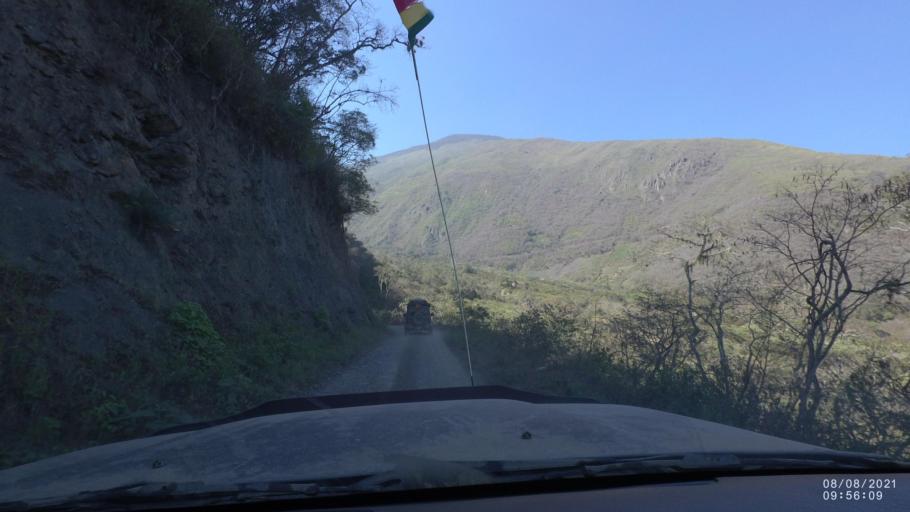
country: BO
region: La Paz
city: Quime
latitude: -16.6370
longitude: -66.7270
